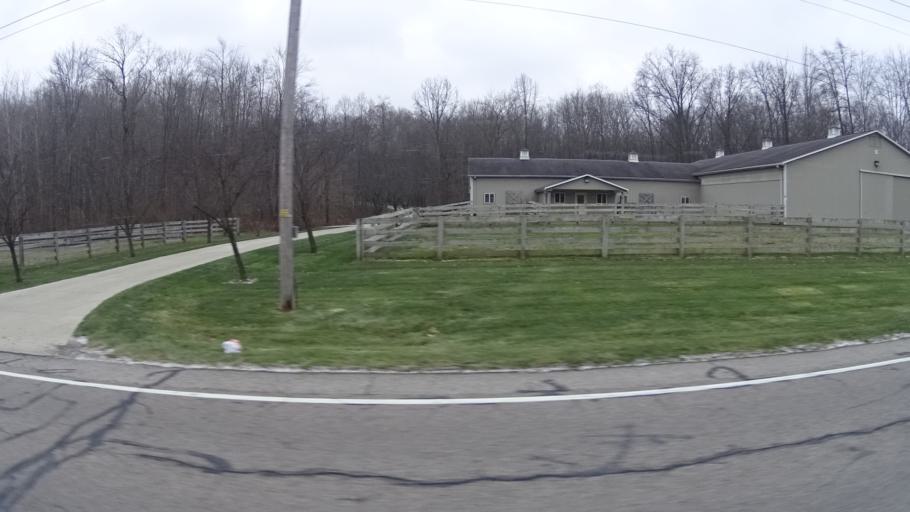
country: US
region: Ohio
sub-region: Lorain County
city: South Amherst
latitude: 41.3385
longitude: -82.2618
